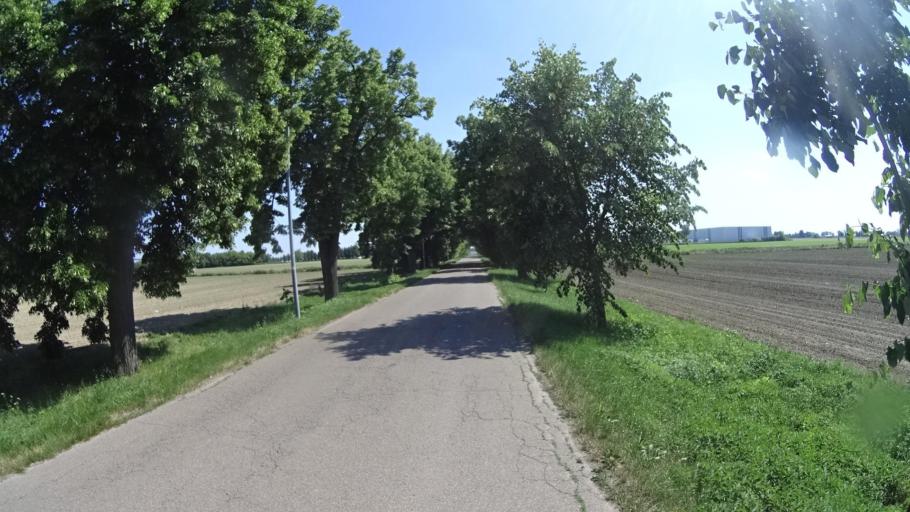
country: PL
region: Masovian Voivodeship
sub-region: Powiat warszawski zachodni
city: Jozefow
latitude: 52.2157
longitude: 20.6718
